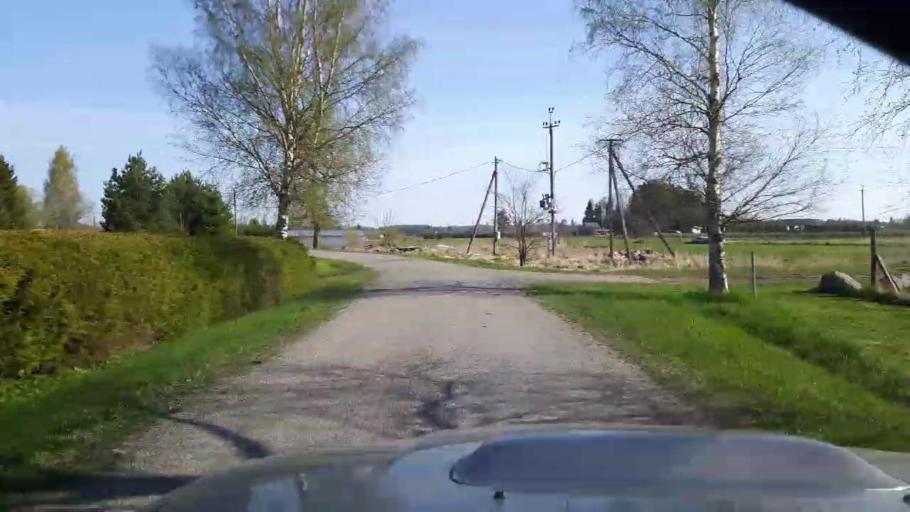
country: EE
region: Paernumaa
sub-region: Tootsi vald
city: Tootsi
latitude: 58.4904
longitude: 24.9061
